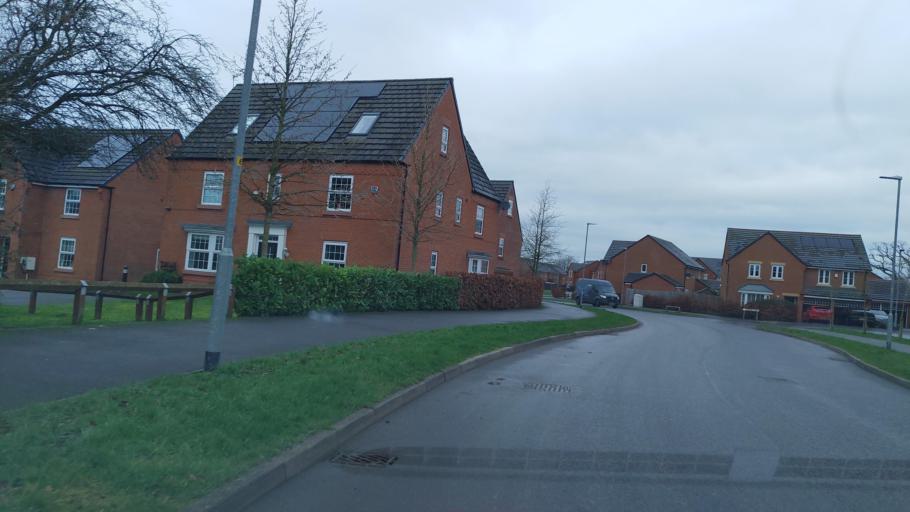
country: GB
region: England
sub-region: Lancashire
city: Clayton-le-Woods
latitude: 53.7006
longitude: -2.6702
